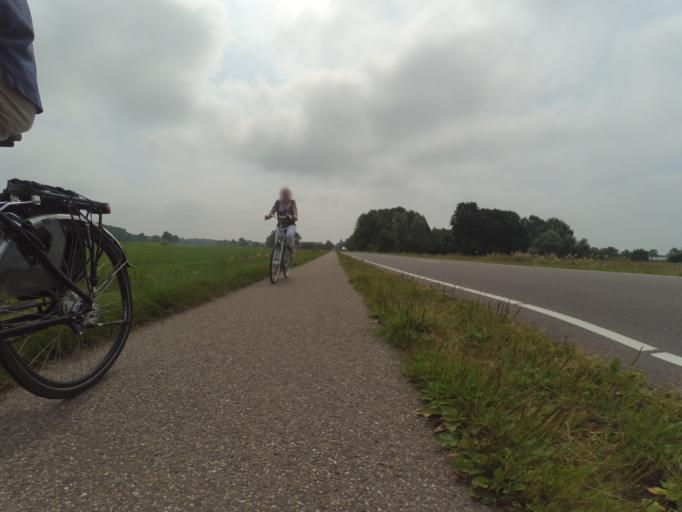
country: NL
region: Gelderland
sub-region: Gemeente Ede
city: Lunteren
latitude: 52.1043
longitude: 5.6054
